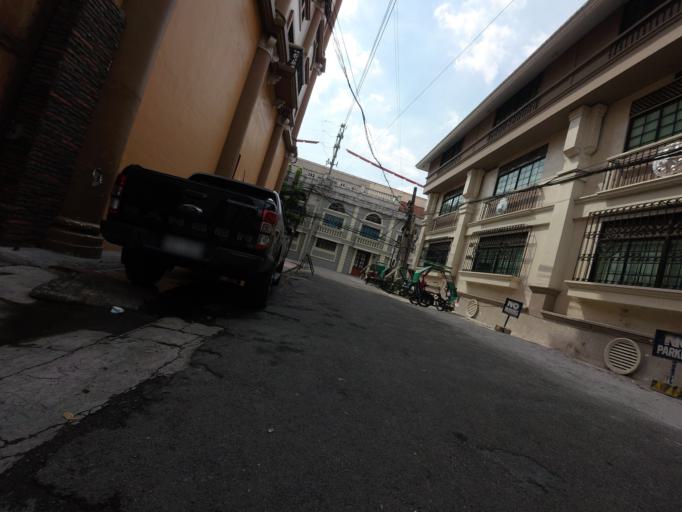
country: PH
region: Metro Manila
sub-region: City of Manila
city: Port Area
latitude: 14.5872
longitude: 120.9776
